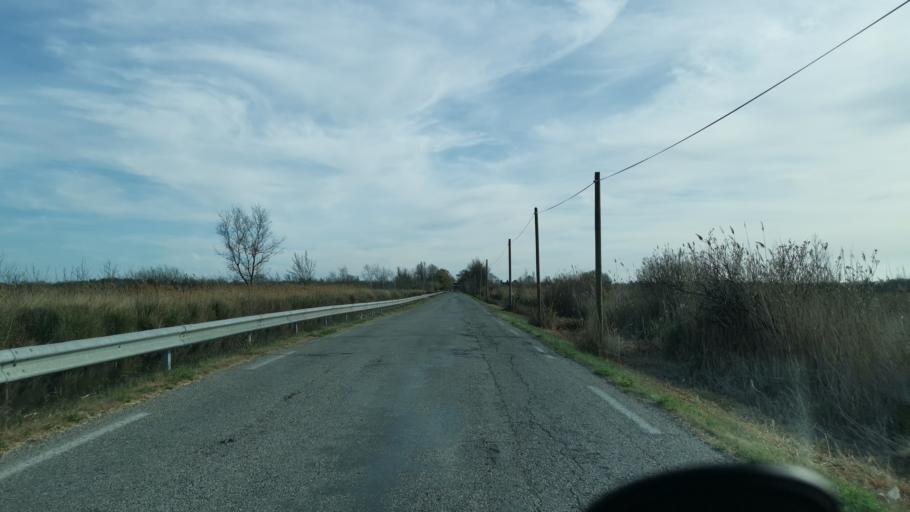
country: FR
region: Provence-Alpes-Cote d'Azur
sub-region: Departement des Bouches-du-Rhone
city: Arles
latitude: 43.6289
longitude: 4.7113
